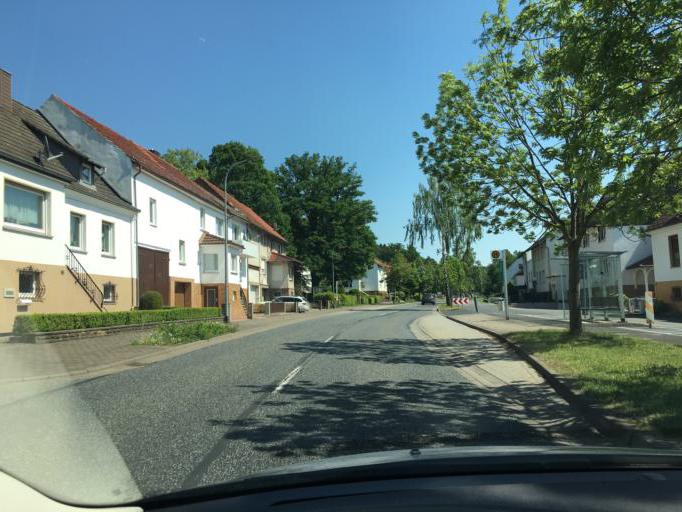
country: DE
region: Hesse
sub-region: Regierungsbezirk Kassel
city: Ronshausen
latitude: 50.9474
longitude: 9.8722
